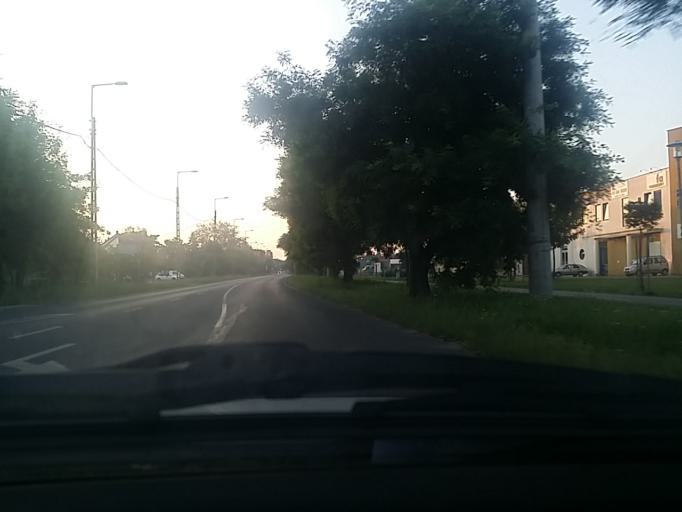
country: HU
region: Budapest
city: Budapest XVII. keruelet
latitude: 47.4743
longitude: 19.2711
